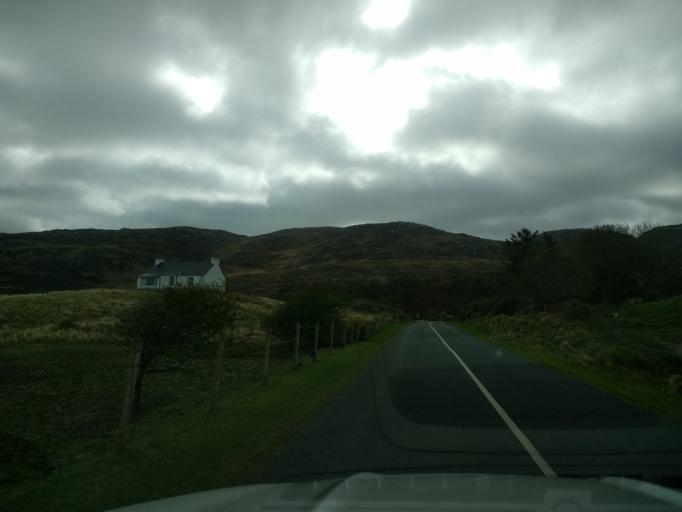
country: IE
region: Ulster
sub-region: County Donegal
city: Ramelton
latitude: 55.1873
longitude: -7.6083
